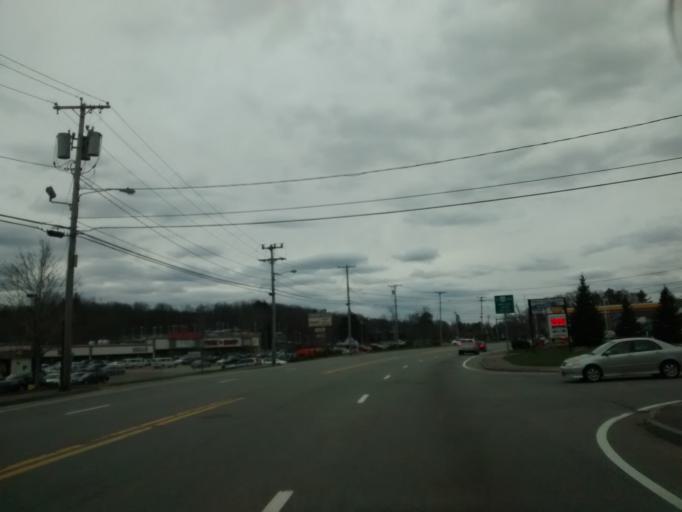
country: US
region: Massachusetts
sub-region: Worcester County
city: Auburn
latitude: 42.1839
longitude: -71.8586
